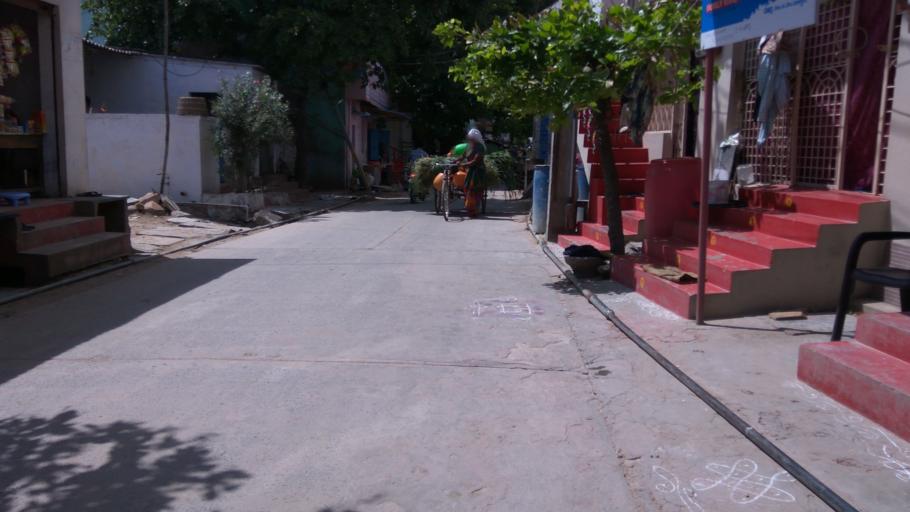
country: IN
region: Andhra Pradesh
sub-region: Prakasam
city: Markapur
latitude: 15.7436
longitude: 79.2708
